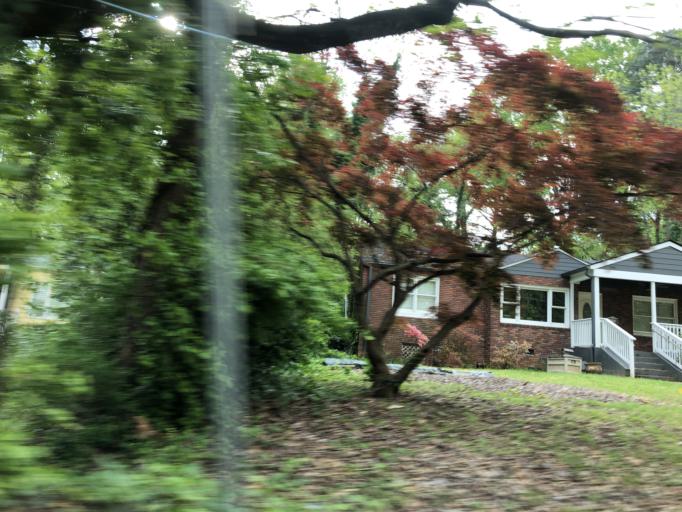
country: US
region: Georgia
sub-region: DeKalb County
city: North Druid Hills
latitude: 33.8128
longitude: -84.3403
